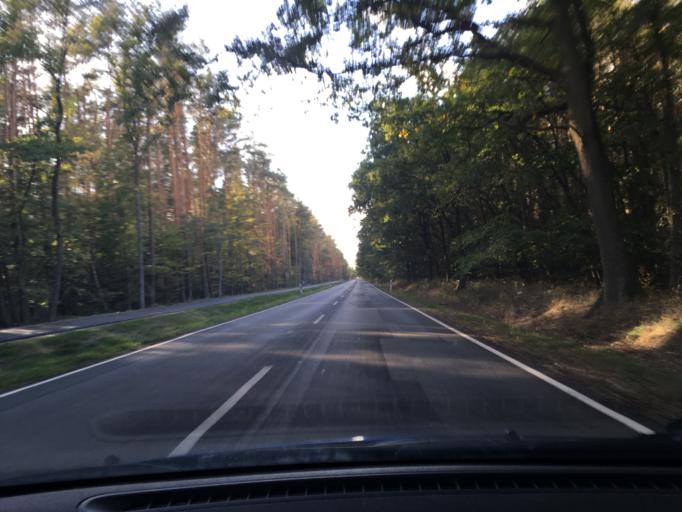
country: DE
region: Mecklenburg-Vorpommern
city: Boizenburg
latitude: 53.3819
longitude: 10.8706
